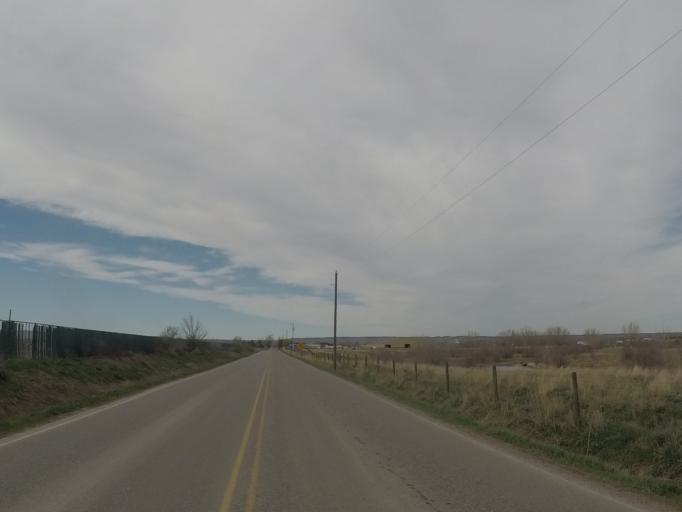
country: US
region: Montana
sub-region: Yellowstone County
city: Laurel
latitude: 45.7140
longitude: -108.6587
